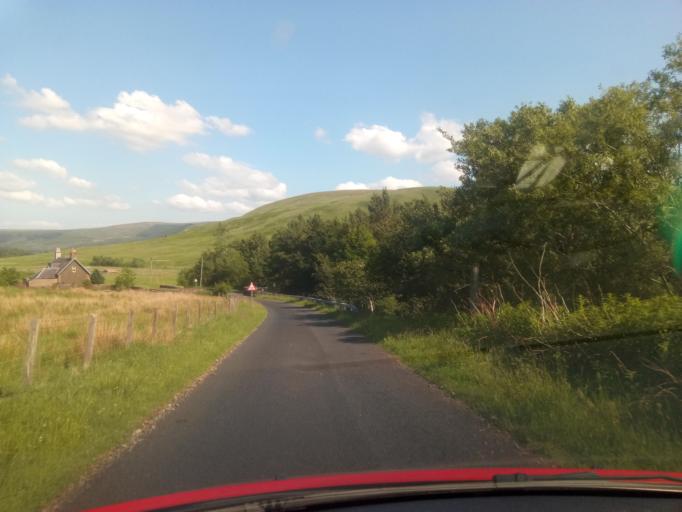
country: GB
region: Scotland
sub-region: The Scottish Borders
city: Peebles
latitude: 55.4959
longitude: -3.2405
